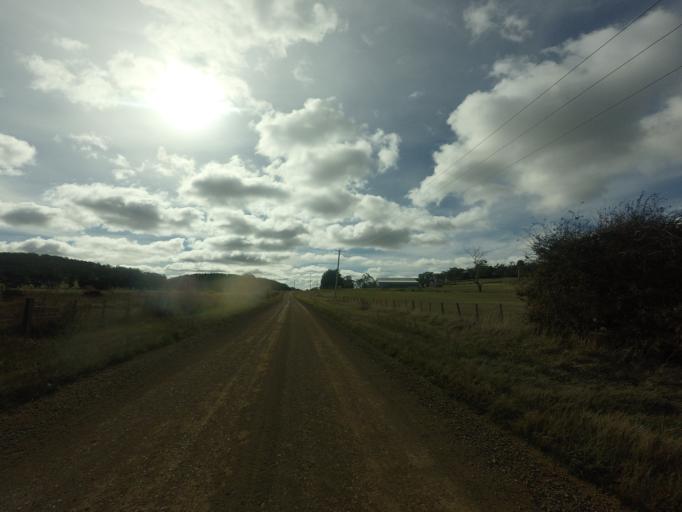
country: AU
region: Tasmania
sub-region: Brighton
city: Bridgewater
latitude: -42.4009
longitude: 147.3911
